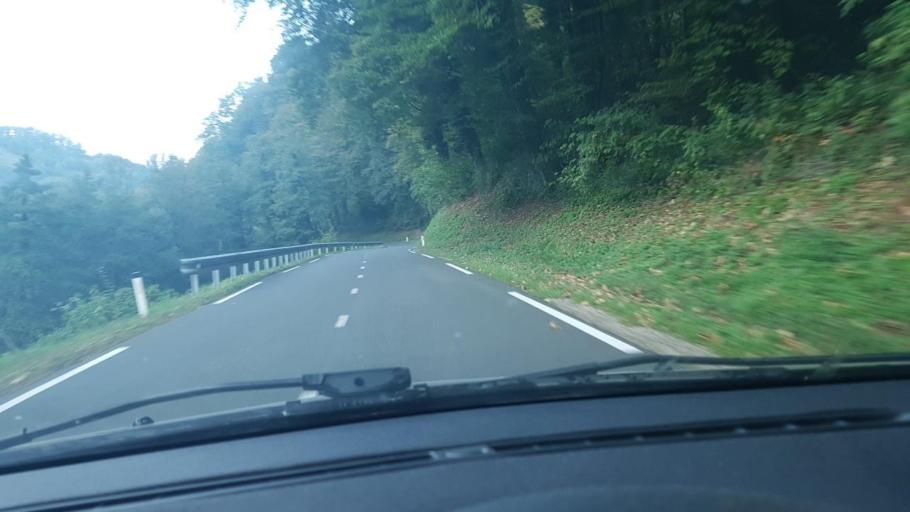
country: SI
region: Majsperk
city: Majsperk
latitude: 46.3175
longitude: 15.7186
